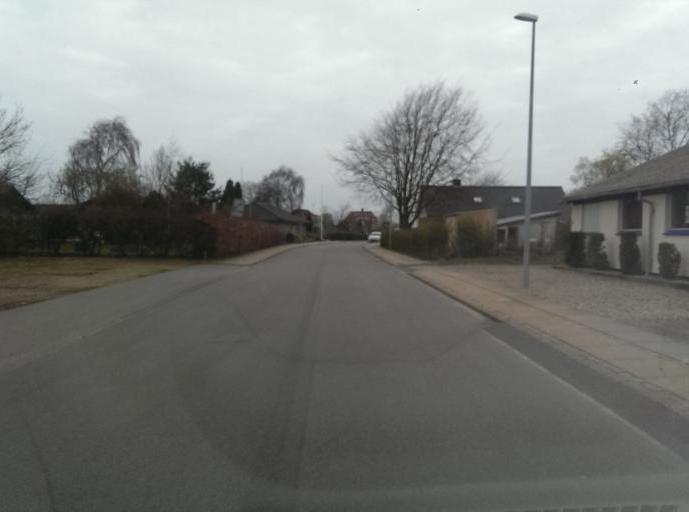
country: DK
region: South Denmark
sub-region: Esbjerg Kommune
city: Bramming
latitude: 55.4647
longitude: 8.6922
